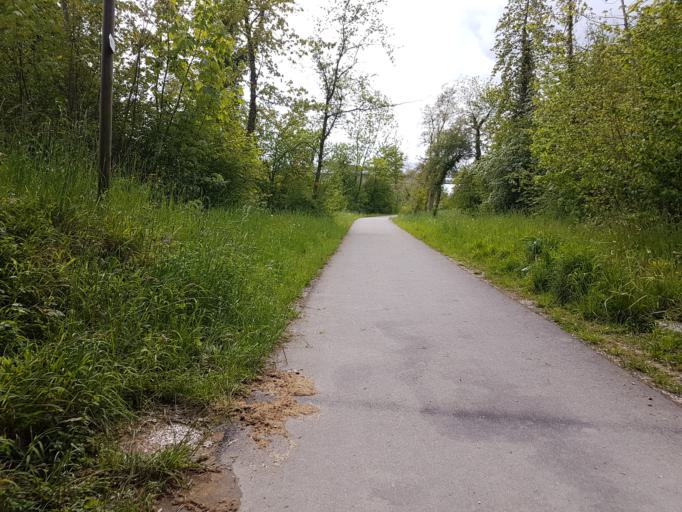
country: CH
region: Aargau
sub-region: Bezirk Lenzburg
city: Niederlenz
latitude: 47.4176
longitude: 8.1601
